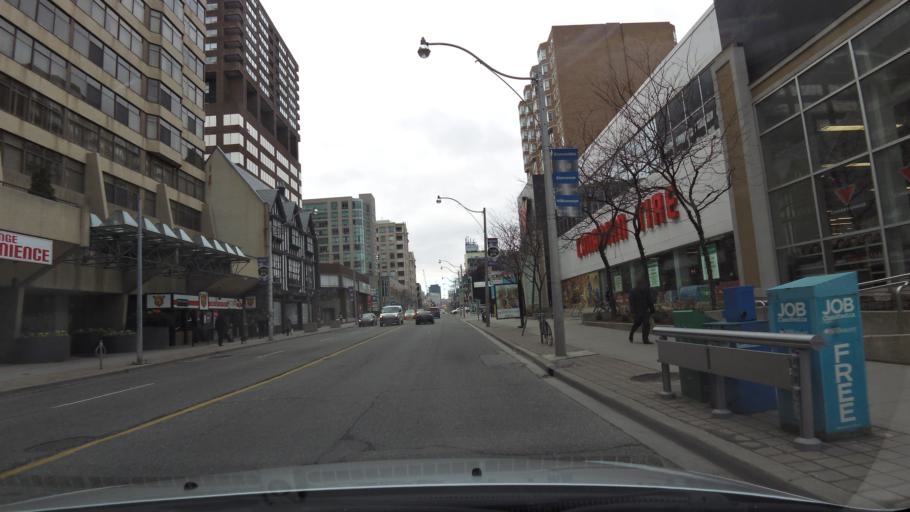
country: CA
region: Ontario
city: Toronto
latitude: 43.6734
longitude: -79.3880
